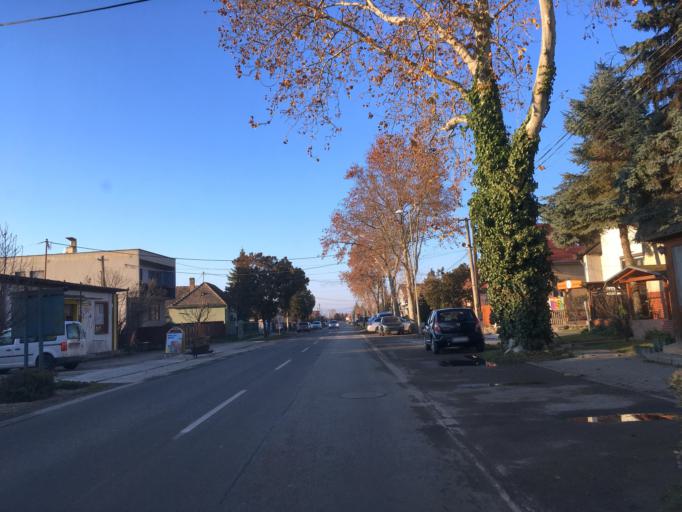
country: SK
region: Trnavsky
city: Gabcikovo
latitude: 47.8945
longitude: 17.5757
